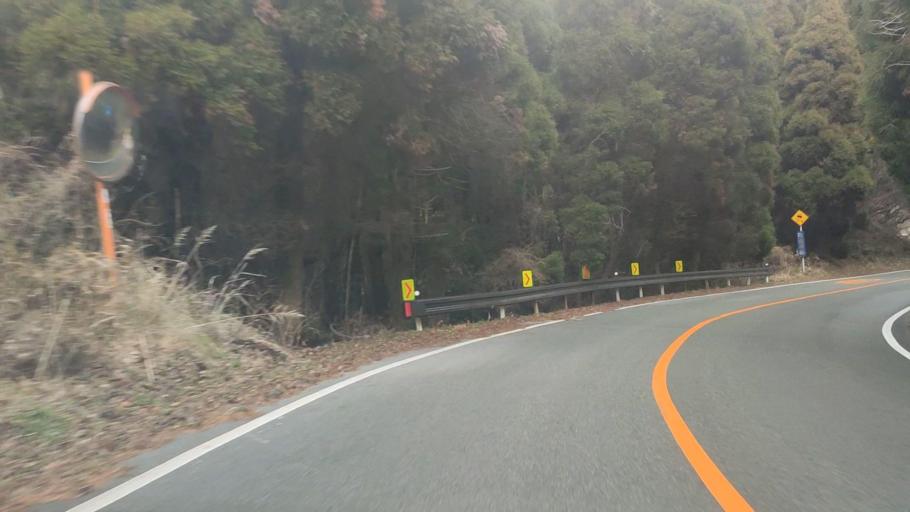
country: JP
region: Kumamoto
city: Aso
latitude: 32.9065
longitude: 131.1442
